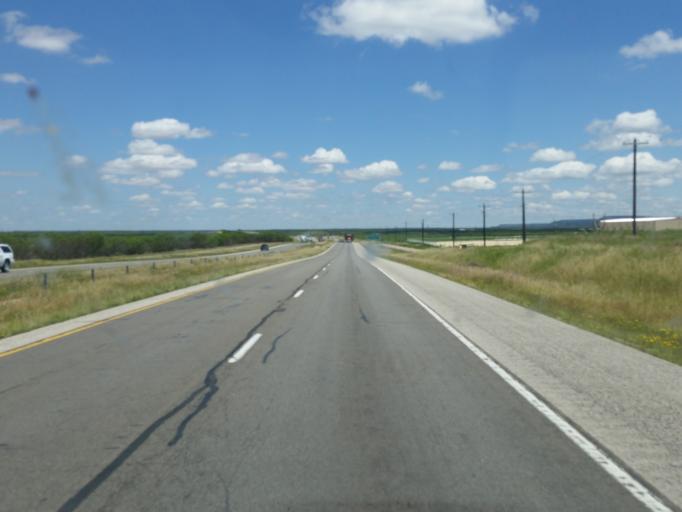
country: US
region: Texas
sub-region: Nolan County
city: Sweetwater
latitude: 32.4939
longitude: -100.2591
